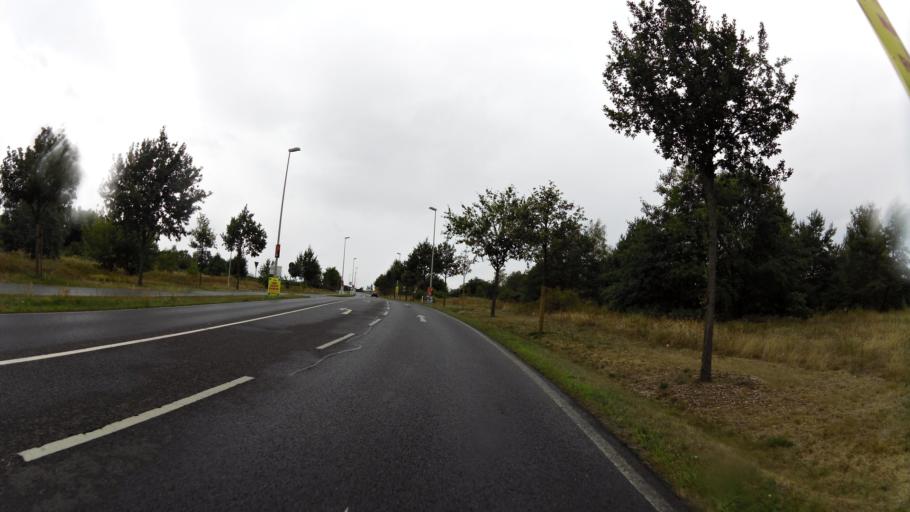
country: DE
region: Brandenburg
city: Cottbus
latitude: 51.7713
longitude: 14.3169
